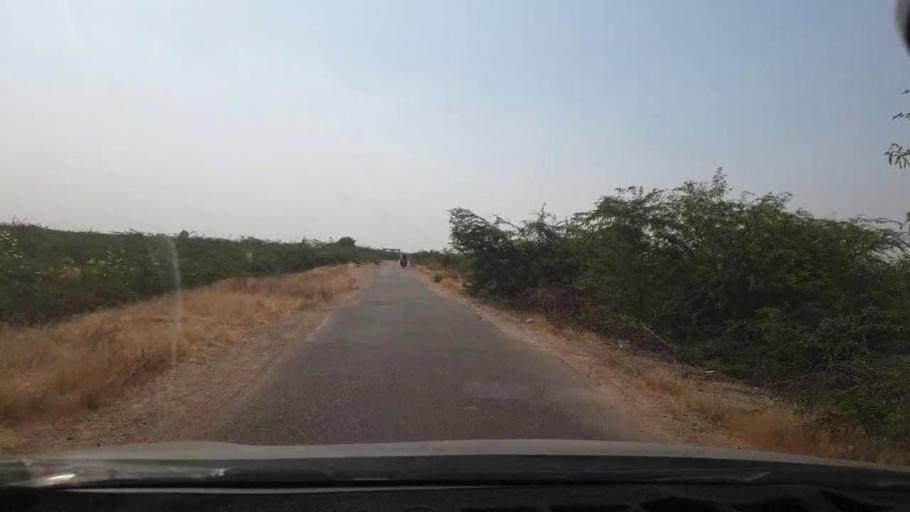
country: PK
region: Sindh
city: Malir Cantonment
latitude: 25.1028
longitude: 67.1965
